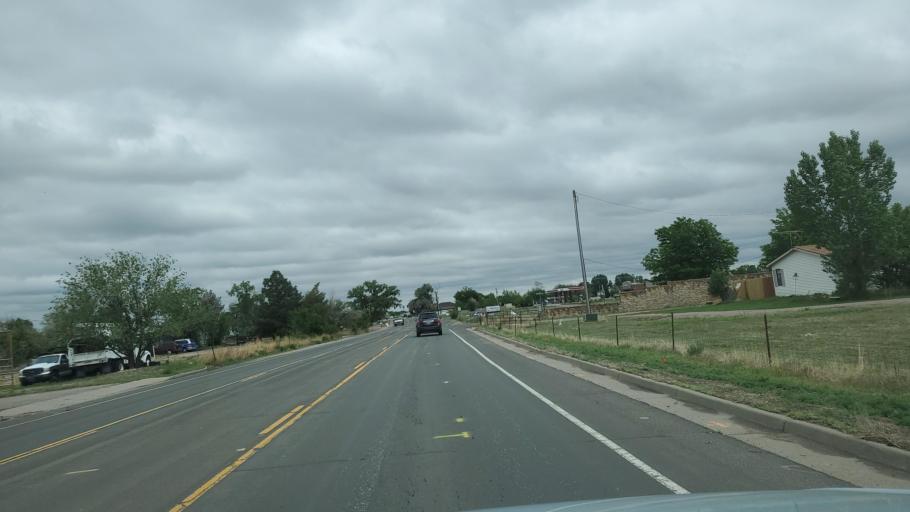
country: US
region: Colorado
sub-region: Adams County
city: Todd Creek
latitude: 39.9143
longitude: -104.8507
